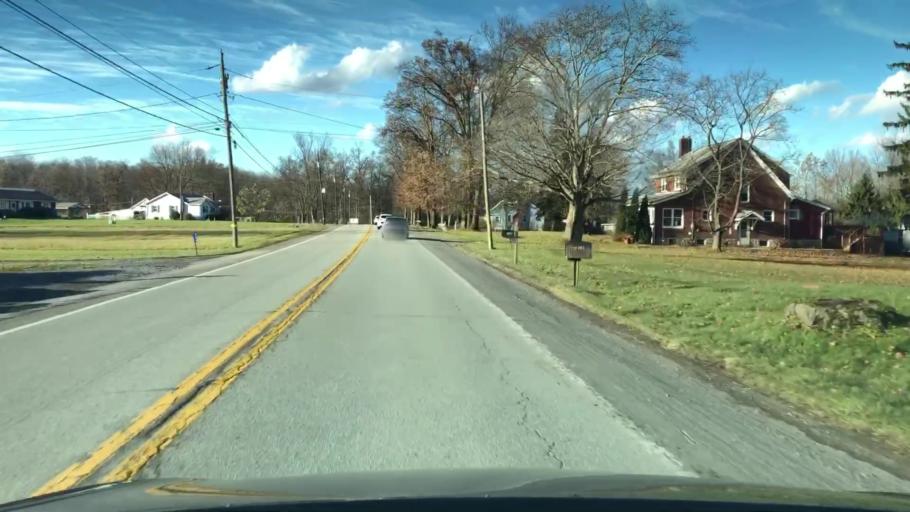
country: US
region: Pennsylvania
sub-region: Butler County
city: Saxonburg
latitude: 40.7467
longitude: -79.7694
